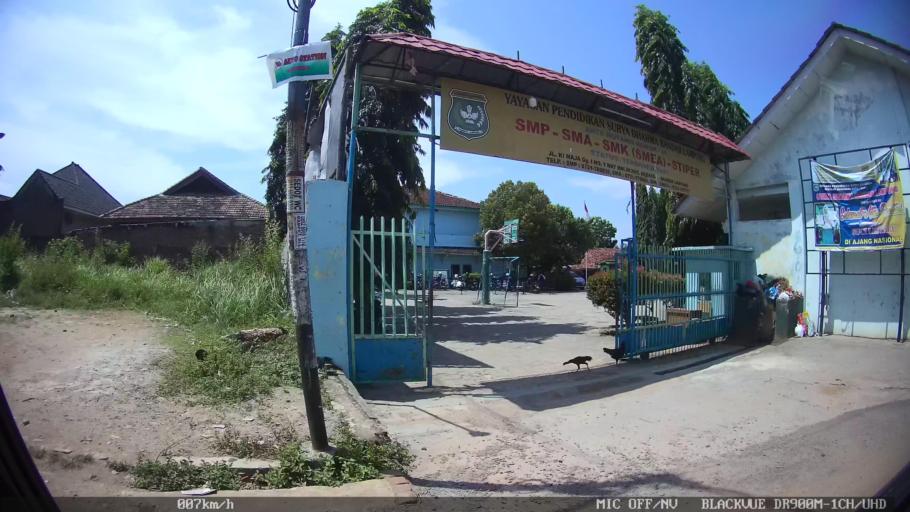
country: ID
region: Lampung
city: Kedaton
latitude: -5.3840
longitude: 105.2674
